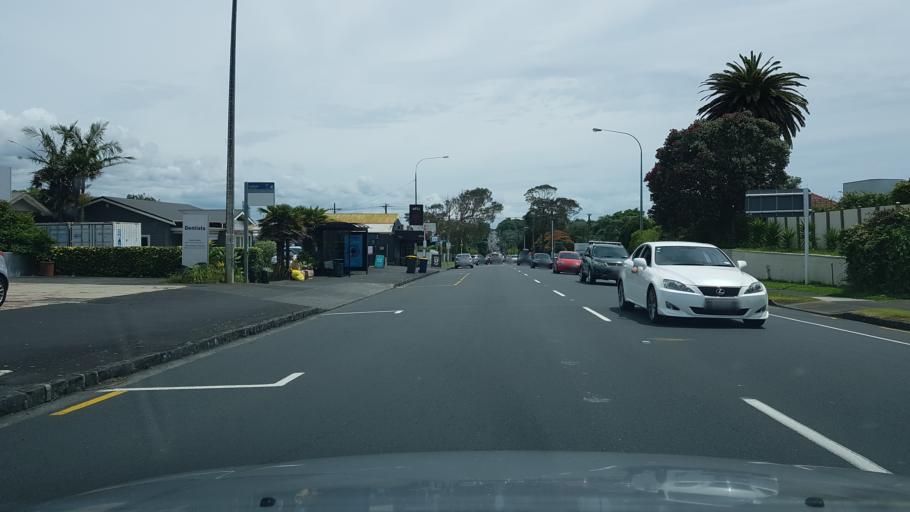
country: NZ
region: Auckland
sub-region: Auckland
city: North Shore
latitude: -36.8072
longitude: 174.7896
